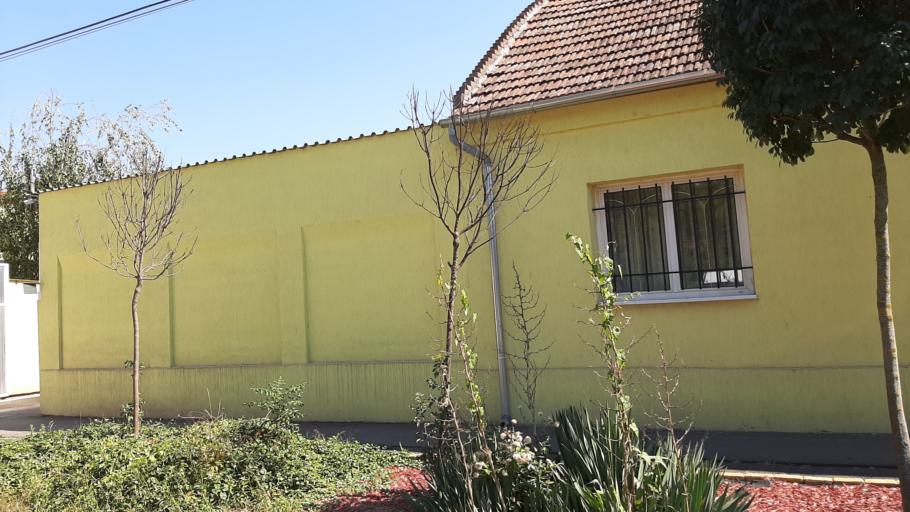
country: HU
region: Csongrad
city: Szeged
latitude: 46.2399
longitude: 20.1284
